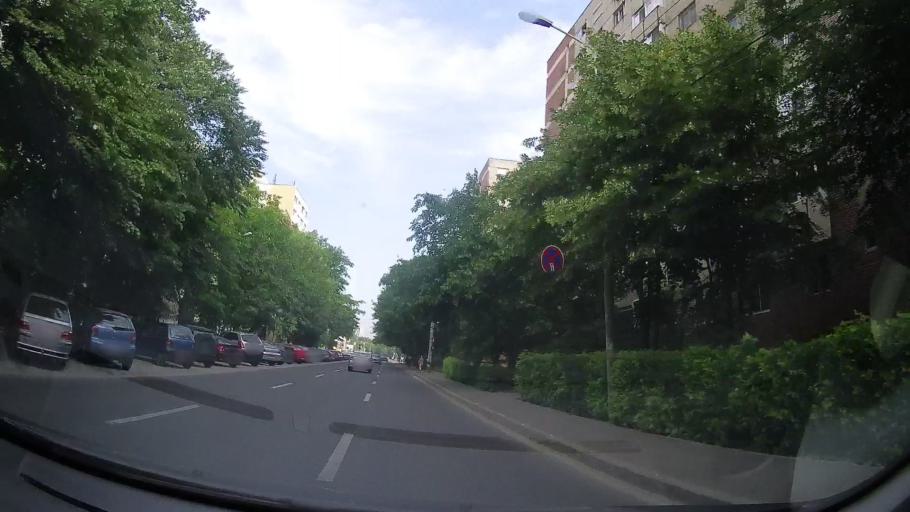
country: RO
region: Timis
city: Timisoara
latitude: 45.7443
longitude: 21.2420
